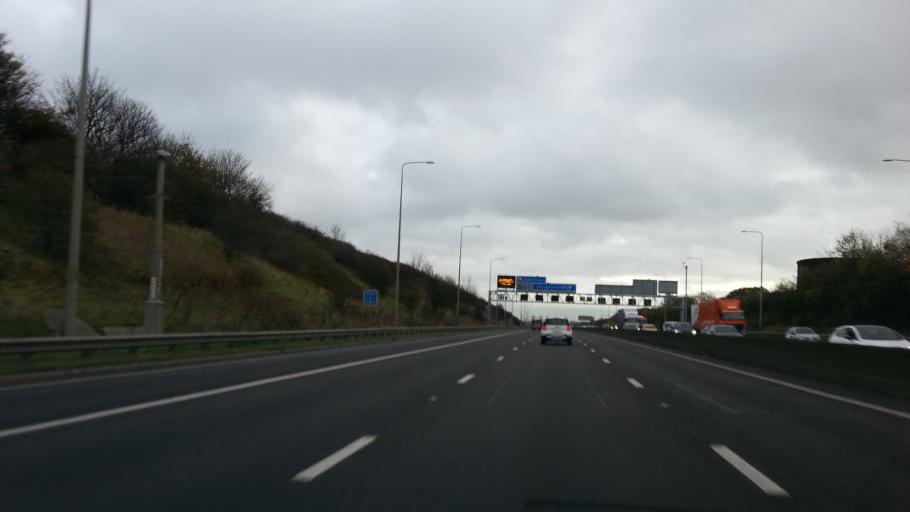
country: GB
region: England
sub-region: City and Borough of Leeds
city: Morley
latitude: 53.7334
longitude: -1.6127
